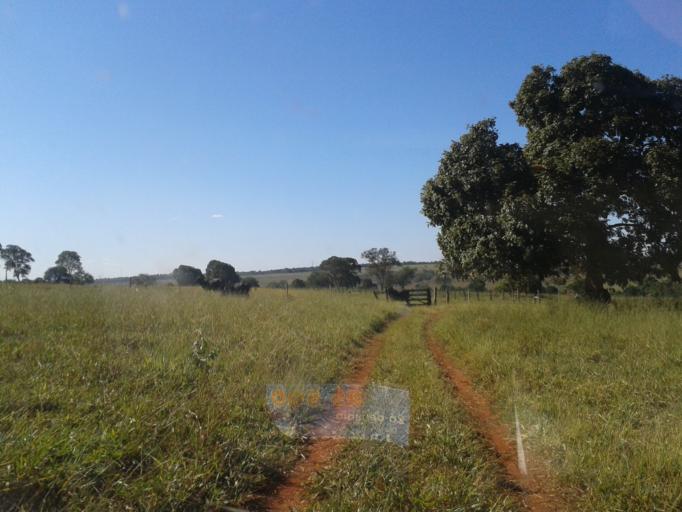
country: BR
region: Minas Gerais
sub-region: Santa Vitoria
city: Santa Vitoria
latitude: -19.0386
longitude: -50.3799
